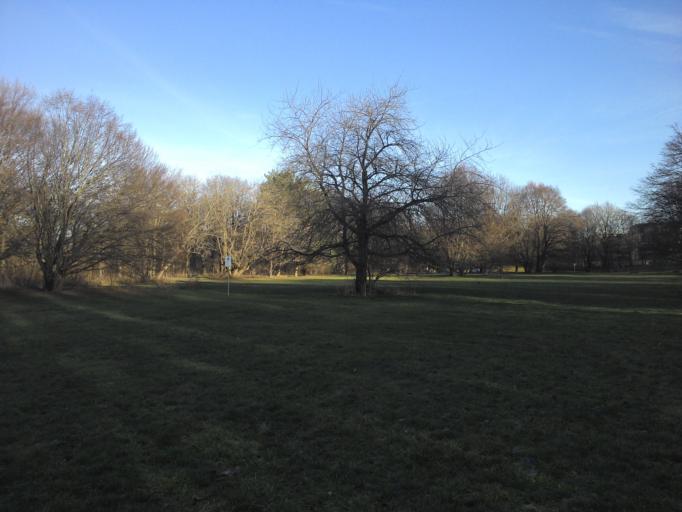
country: DE
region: Bavaria
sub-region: Upper Bavaria
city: Pasing
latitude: 48.1477
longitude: 11.5146
